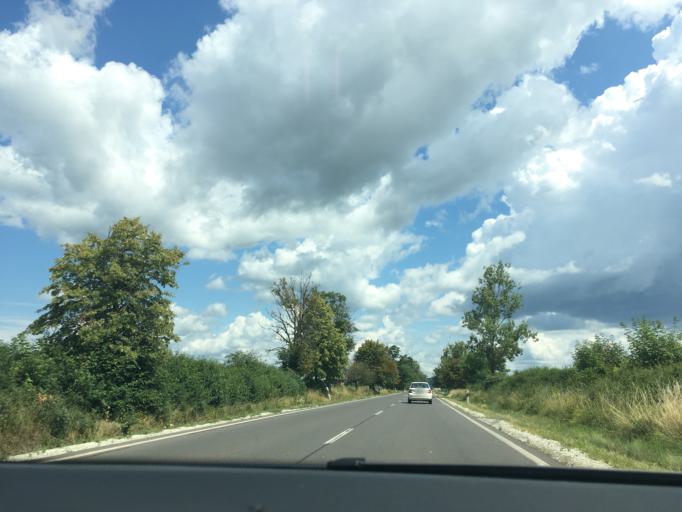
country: HU
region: Borsod-Abauj-Zemplen
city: Olaszliszka
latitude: 48.2338
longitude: 21.4051
